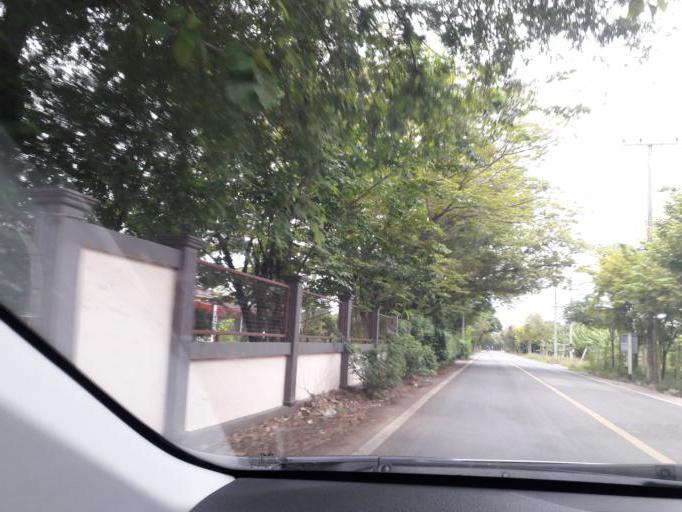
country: TH
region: Samut Sakhon
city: Ban Phaeo
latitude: 13.6230
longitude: 100.0205
